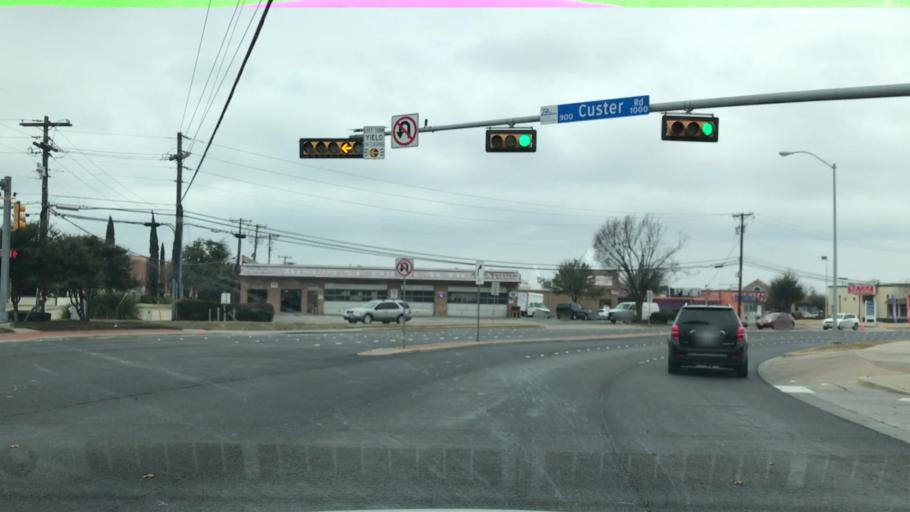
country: US
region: Texas
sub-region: Dallas County
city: Richardson
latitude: 32.9609
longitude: -96.7347
